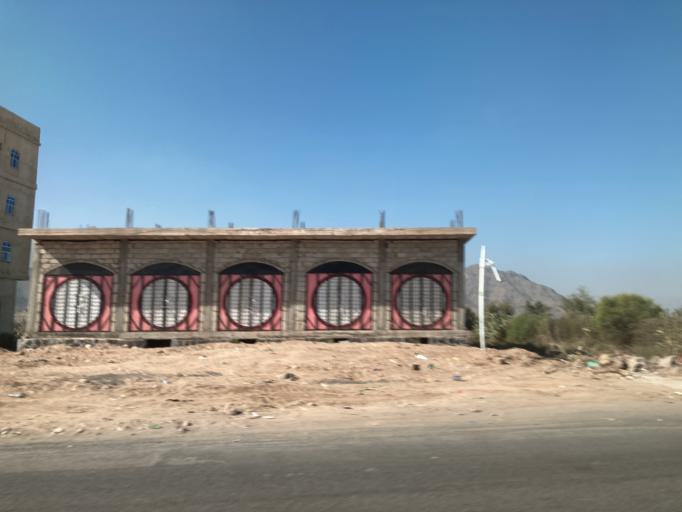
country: YE
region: Ad Dali'
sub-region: Qa'atabah
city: Qa`tabah
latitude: 13.8122
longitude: 44.7213
